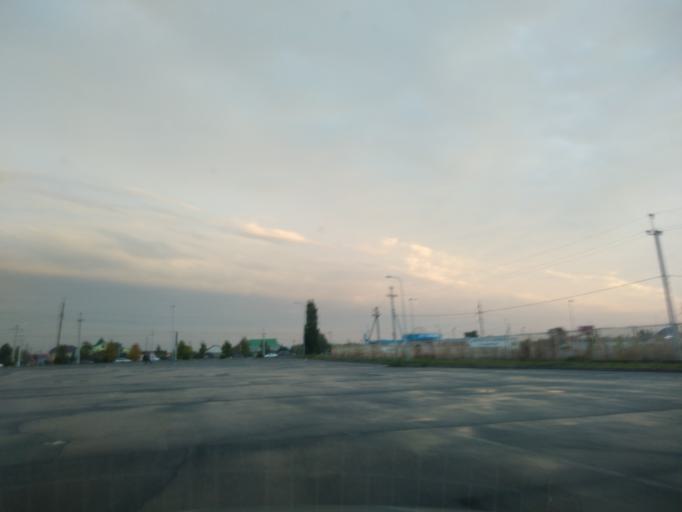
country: RU
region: Lipetsk
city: Syrskoye
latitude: 52.5736
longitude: 39.5214
